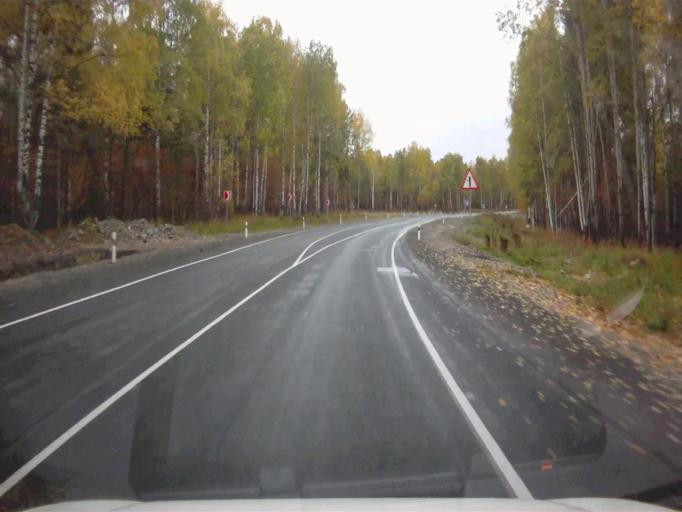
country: RU
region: Chelyabinsk
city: Nyazepetrovsk
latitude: 56.0600
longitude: 59.7313
